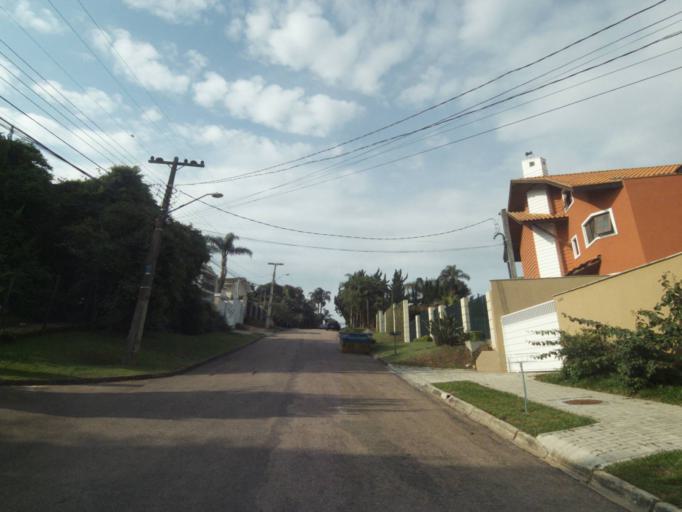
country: BR
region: Parana
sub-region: Curitiba
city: Curitiba
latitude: -25.4154
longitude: -49.3102
